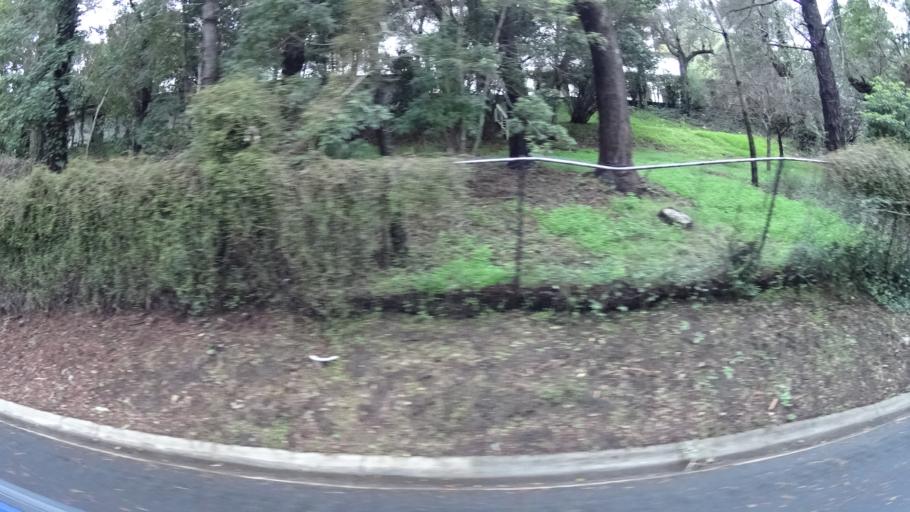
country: US
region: California
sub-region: San Mateo County
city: Hillsborough
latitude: 37.5615
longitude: -122.3644
